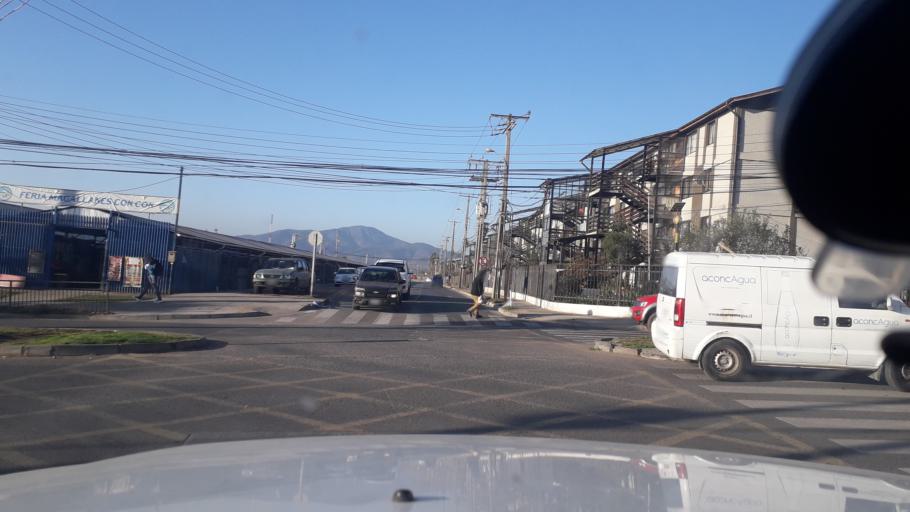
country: CL
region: Valparaiso
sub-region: Provincia de Valparaiso
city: Vina del Mar
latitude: -32.9307
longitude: -71.5180
